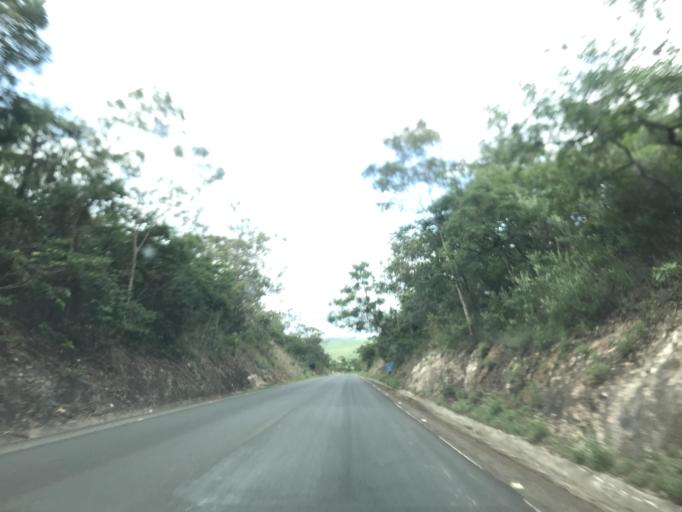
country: BR
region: Goias
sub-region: Vianopolis
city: Vianopolis
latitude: -16.9585
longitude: -48.5983
